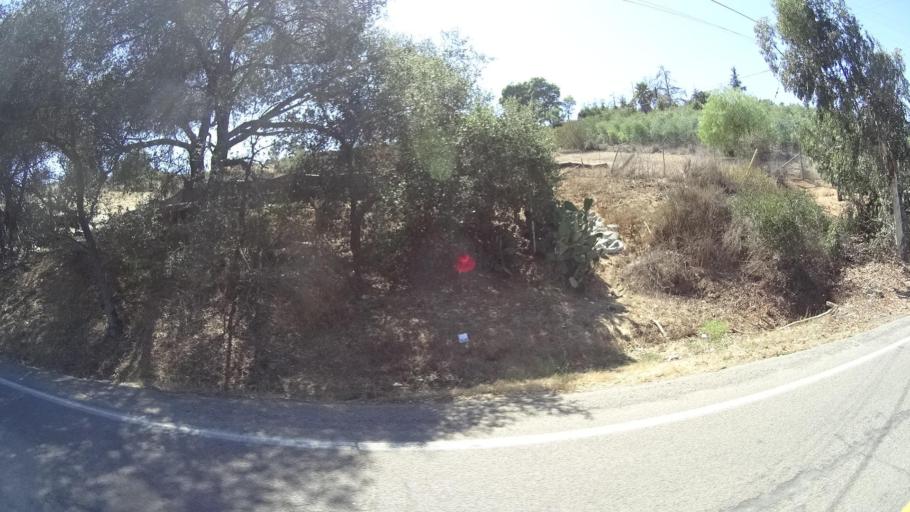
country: US
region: California
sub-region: San Diego County
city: Hidden Meadows
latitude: 33.2800
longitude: -117.1141
